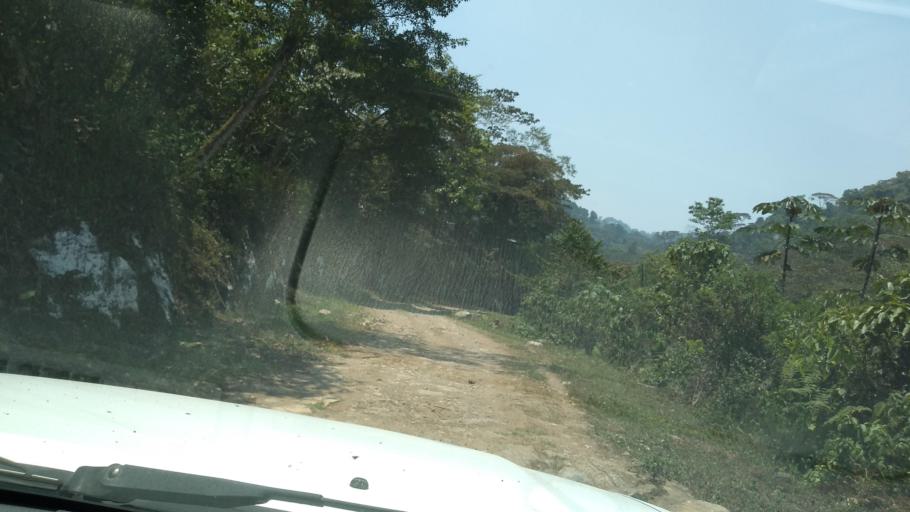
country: MX
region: Veracruz
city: Motzorongo
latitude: 18.6182
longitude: -96.7584
